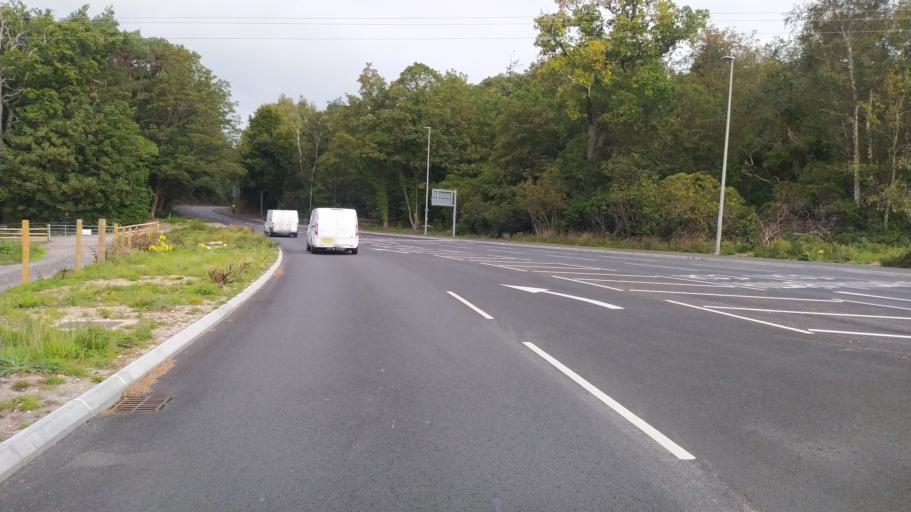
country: GB
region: England
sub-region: Dorset
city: Christchurch
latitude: 50.7648
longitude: -1.8130
